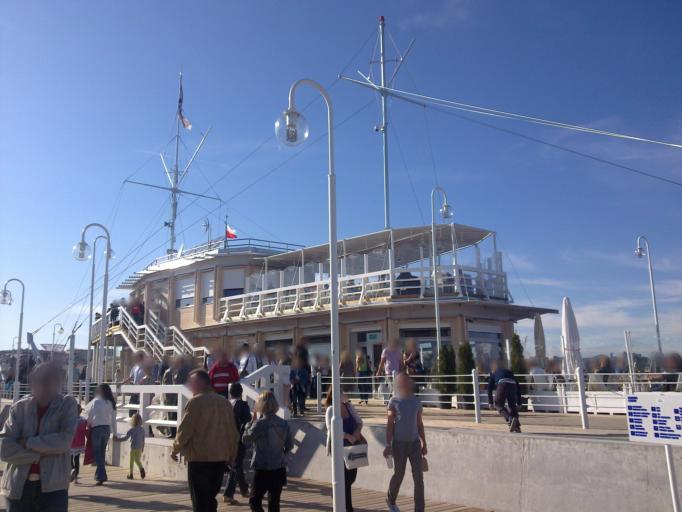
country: PL
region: Pomeranian Voivodeship
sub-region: Sopot
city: Sopot
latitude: 54.4478
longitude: 18.5764
